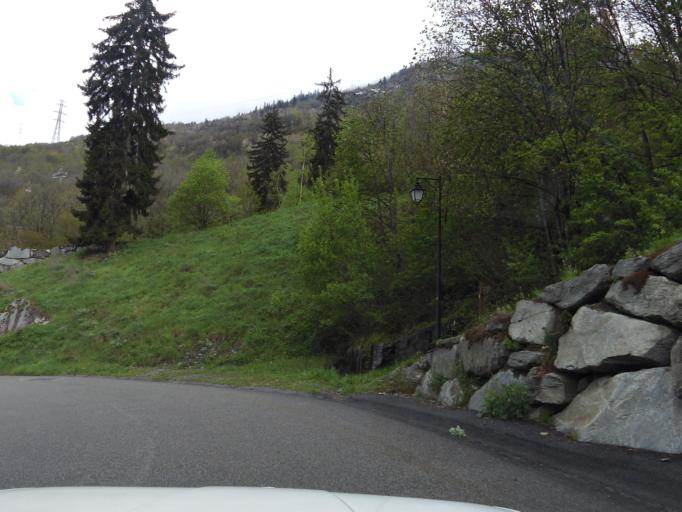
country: FR
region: Rhone-Alpes
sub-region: Departement de la Savoie
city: Saint-Michel-de-Maurienne
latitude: 45.2096
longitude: 6.5500
